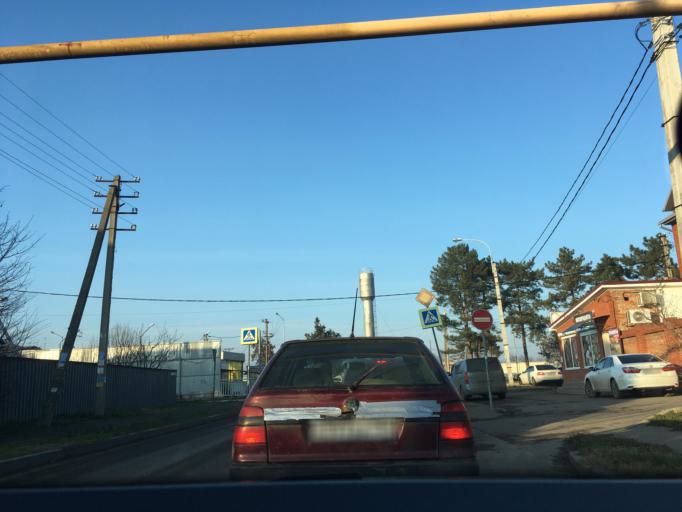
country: RU
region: Krasnodarskiy
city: Krasnodar
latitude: 45.1253
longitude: 39.0139
